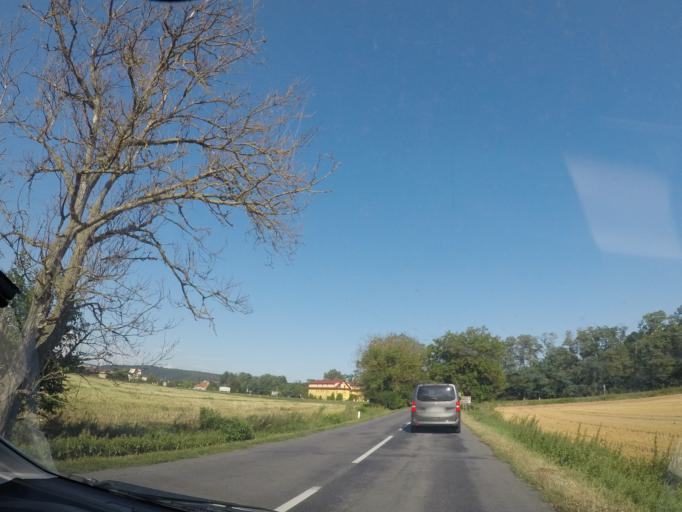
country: SK
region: Banskobystricky
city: Dudince
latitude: 48.1680
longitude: 18.8717
